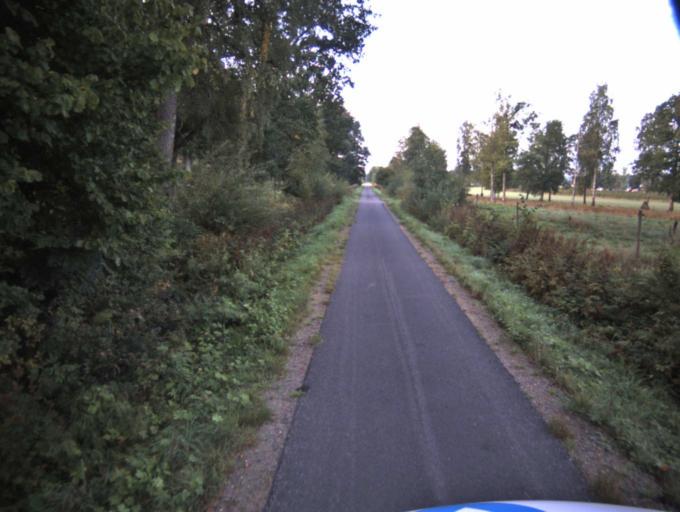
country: SE
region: Vaestra Goetaland
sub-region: Ulricehamns Kommun
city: Ulricehamn
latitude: 57.7242
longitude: 13.4048
